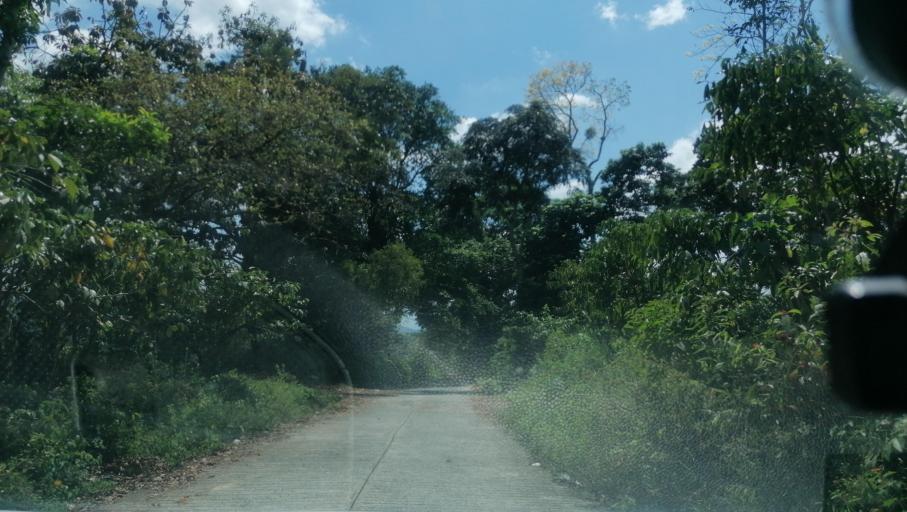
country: MX
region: Chiapas
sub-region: Union Juarez
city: Santo Domingo
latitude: 15.0373
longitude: -92.1436
